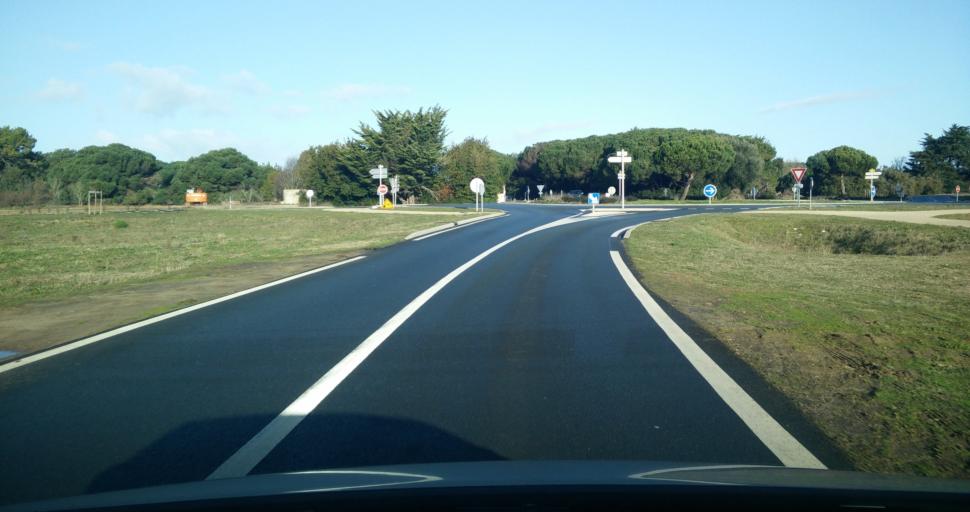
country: FR
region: Poitou-Charentes
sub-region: Departement de la Charente-Maritime
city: La Flotte
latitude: 46.1787
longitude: -1.3330
